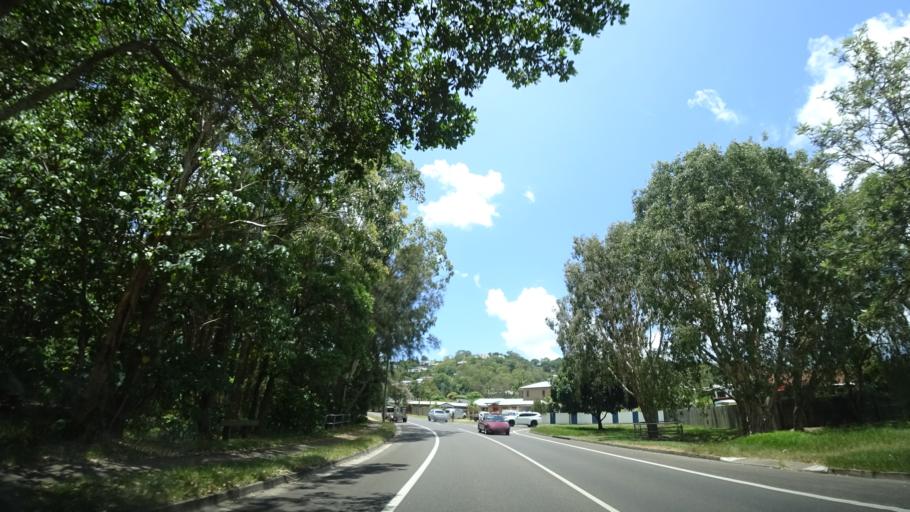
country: AU
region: Queensland
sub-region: Sunshine Coast
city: Coolum Beach
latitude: -26.5346
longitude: 153.0849
